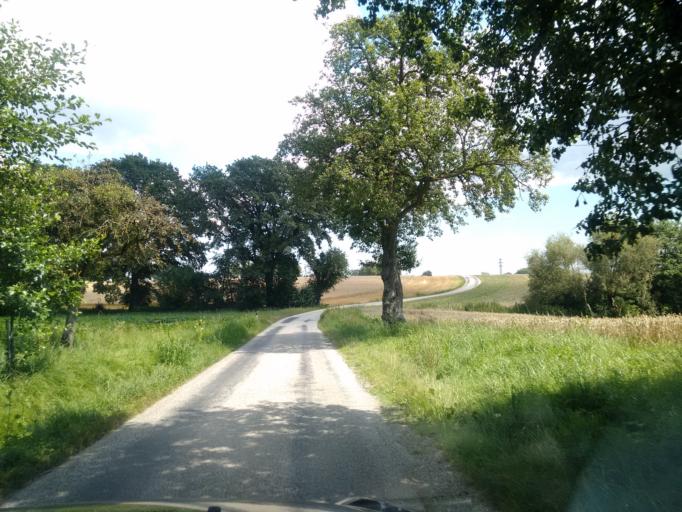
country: AT
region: Upper Austria
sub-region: Wels-Land
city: Gunskirchen
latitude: 48.1761
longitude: 13.9604
